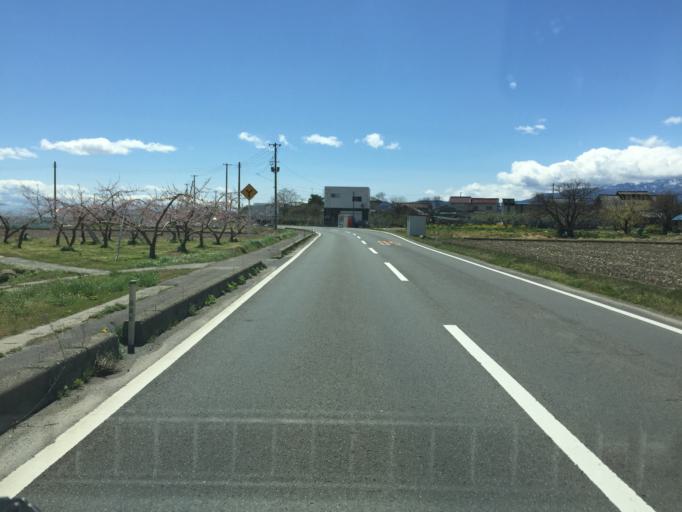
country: JP
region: Fukushima
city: Fukushima-shi
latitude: 37.7953
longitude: 140.4100
